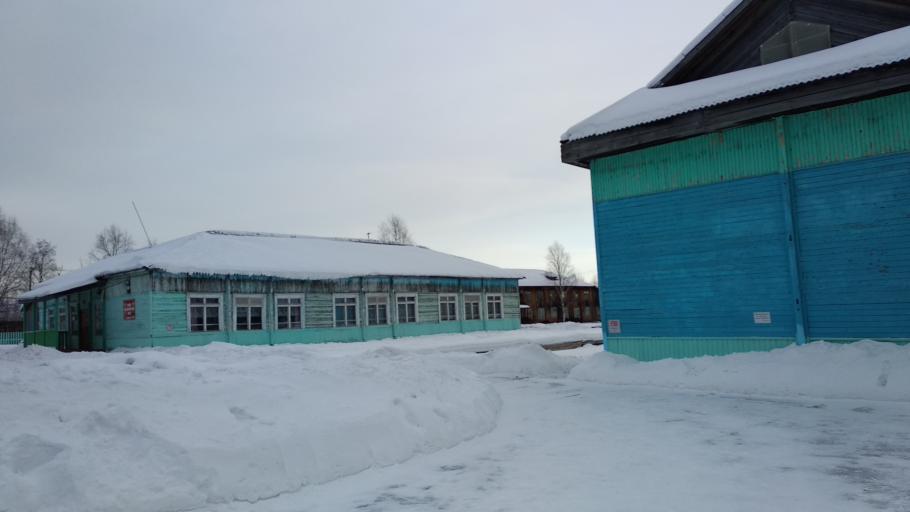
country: RU
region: Sverdlovsk
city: Serov
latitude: 59.9267
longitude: 60.5884
